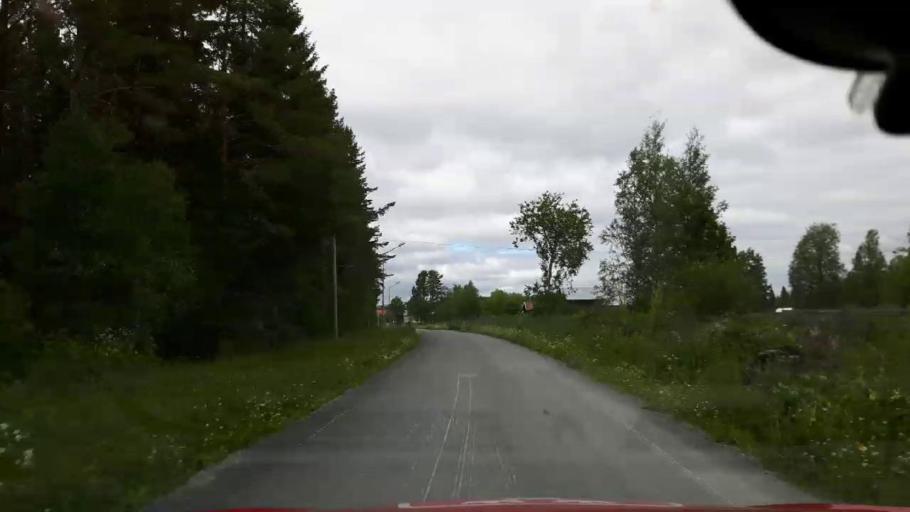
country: SE
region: Jaemtland
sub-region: OEstersunds Kommun
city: Brunflo
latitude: 63.0695
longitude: 14.8936
